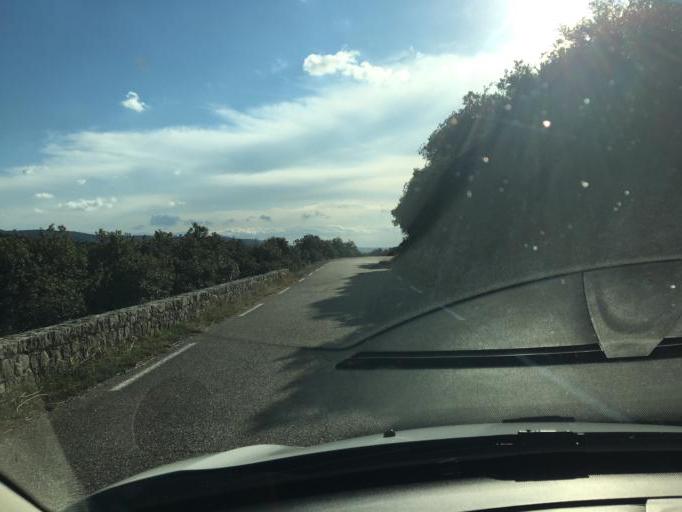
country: FR
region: Provence-Alpes-Cote d'Azur
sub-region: Departement du Vaucluse
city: Villes-sur-Auzon
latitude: 44.0352
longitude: 5.2637
